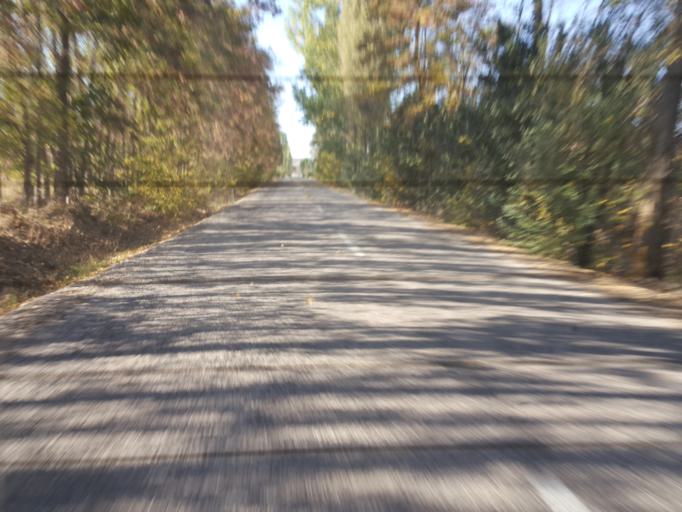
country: TR
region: Corum
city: Seydim
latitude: 40.5562
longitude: 34.7583
